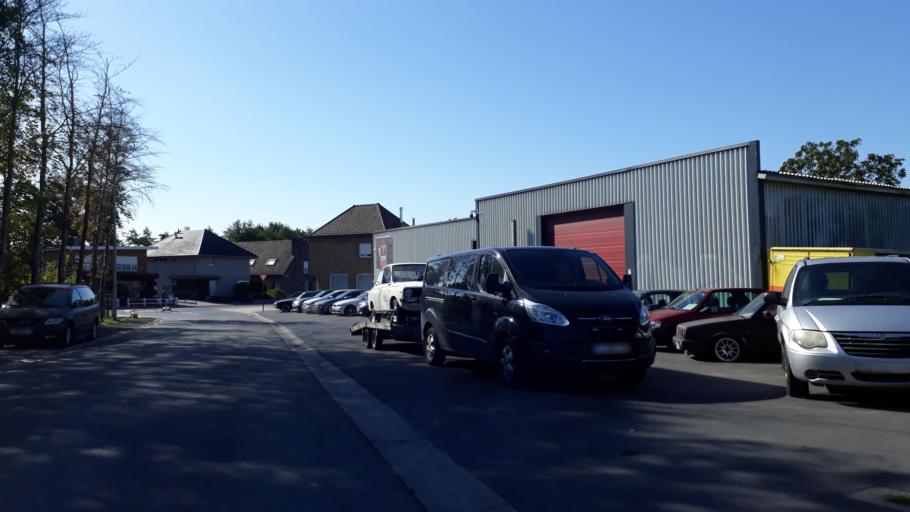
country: BE
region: Flanders
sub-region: Provincie West-Vlaanderen
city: Torhout
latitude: 51.0805
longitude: 3.1192
